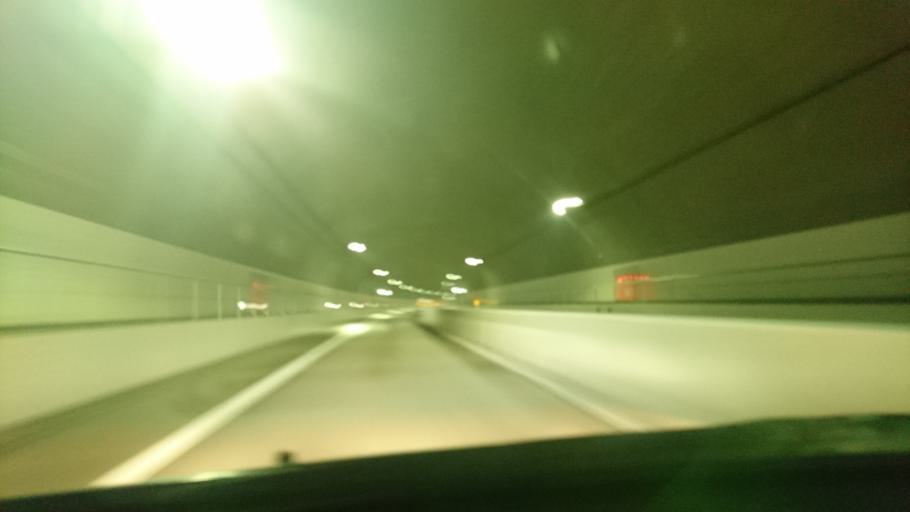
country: JP
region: Iwate
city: Miyako
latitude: 39.8109
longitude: 141.9574
